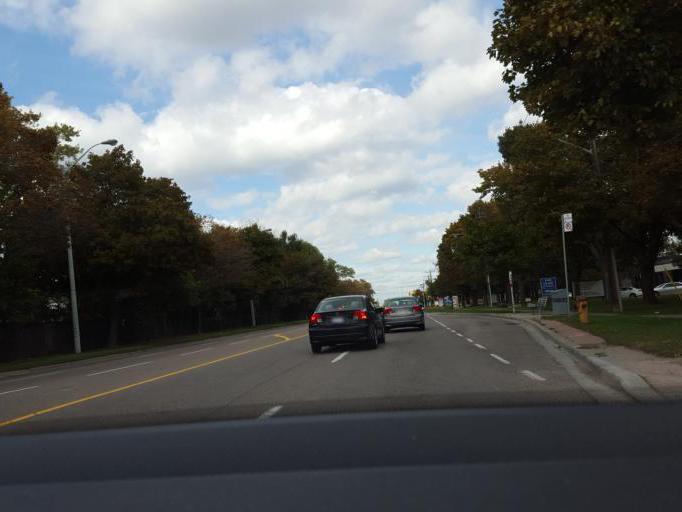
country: CA
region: Ontario
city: Willowdale
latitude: 43.7567
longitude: -79.3608
